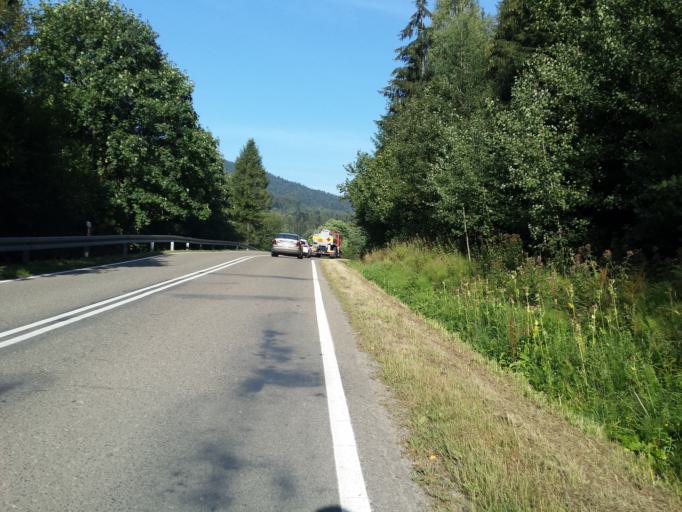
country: PL
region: Subcarpathian Voivodeship
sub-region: Powiat leski
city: Cisna
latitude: 49.2175
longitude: 22.3209
